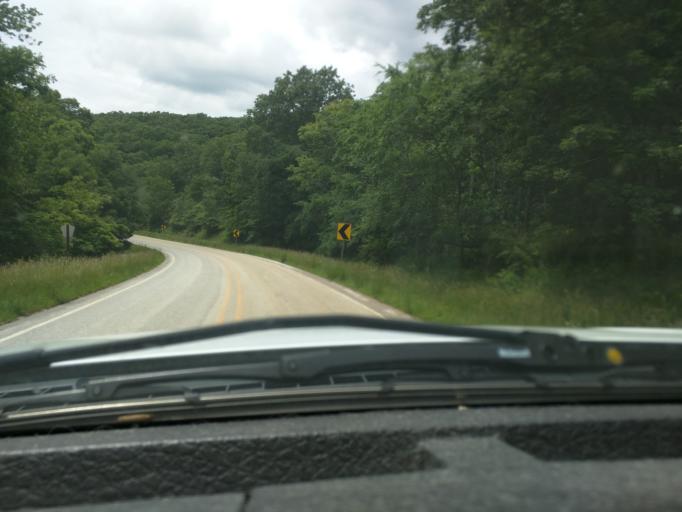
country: US
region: Arkansas
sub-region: Madison County
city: Huntsville
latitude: 35.8655
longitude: -93.5321
